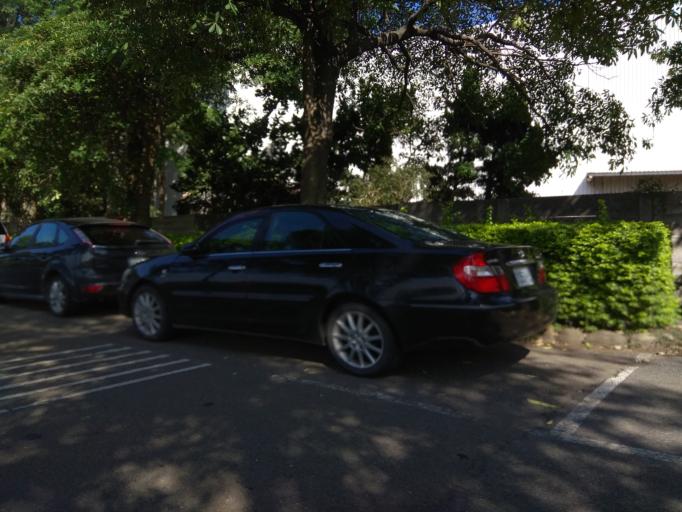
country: TW
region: Taiwan
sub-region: Hsinchu
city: Zhubei
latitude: 24.9793
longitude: 121.0395
